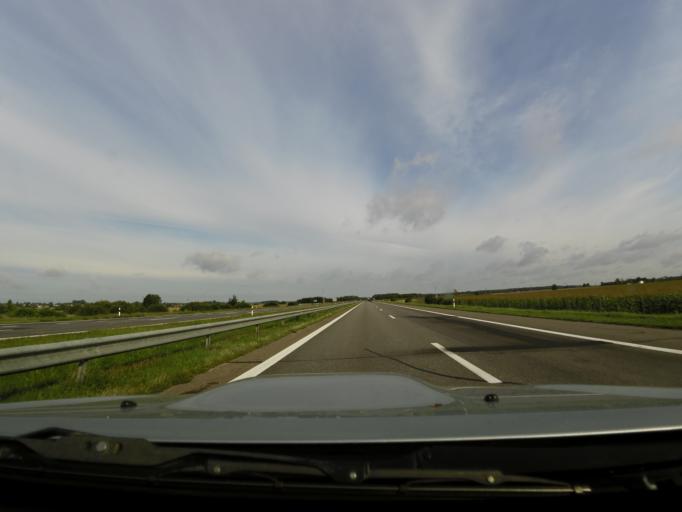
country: LT
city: Sirvintos
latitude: 55.0170
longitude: 24.9111
